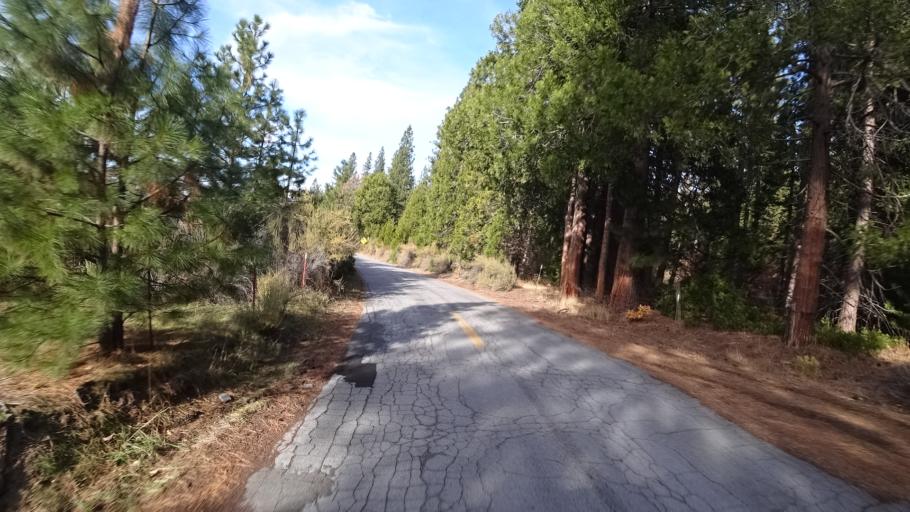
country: US
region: California
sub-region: Siskiyou County
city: Weed
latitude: 41.4479
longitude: -122.3792
